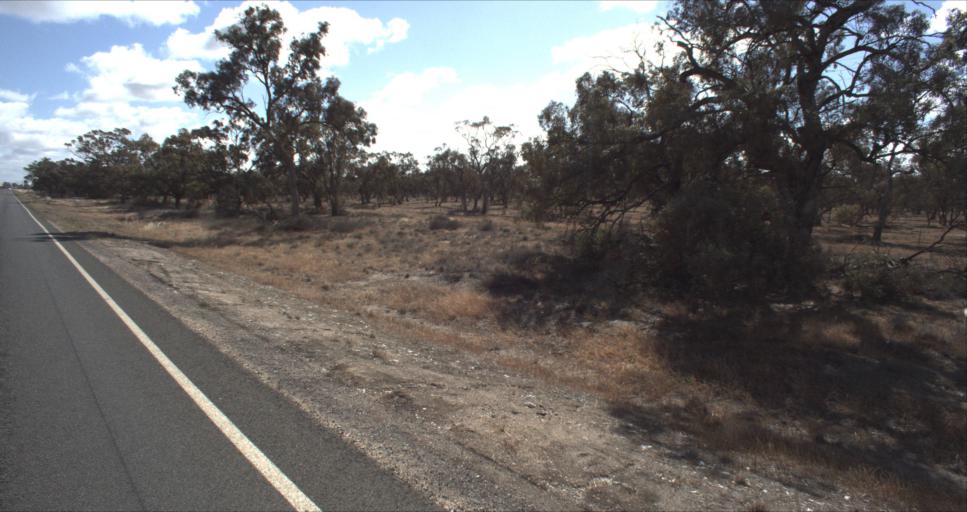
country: AU
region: New South Wales
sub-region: Murrumbidgee Shire
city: Darlington Point
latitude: -34.5250
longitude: 146.1750
